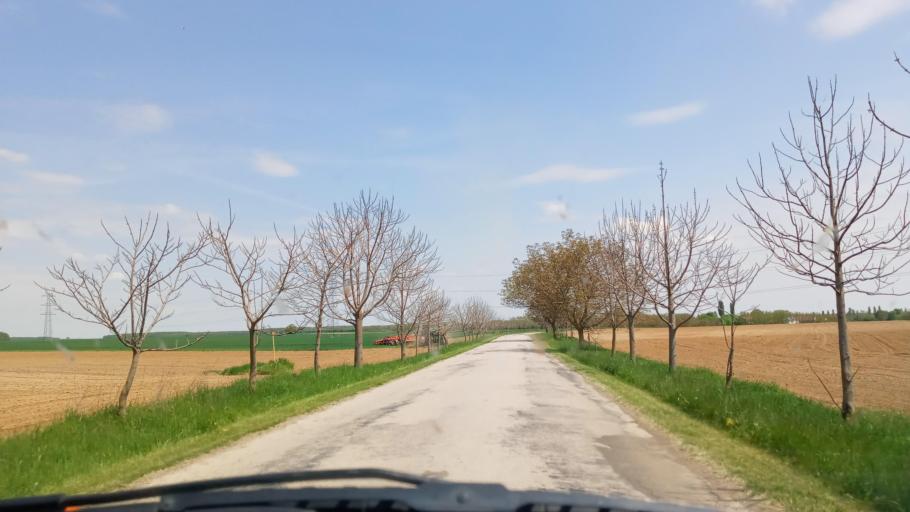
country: HU
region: Baranya
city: Villany
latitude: 45.8829
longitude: 18.4840
